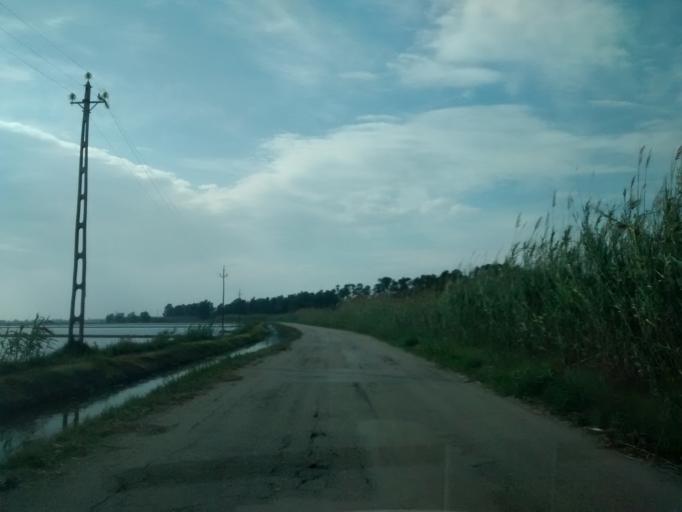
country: ES
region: Catalonia
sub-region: Provincia de Tarragona
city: Deltebre
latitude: 40.6966
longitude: 0.8357
